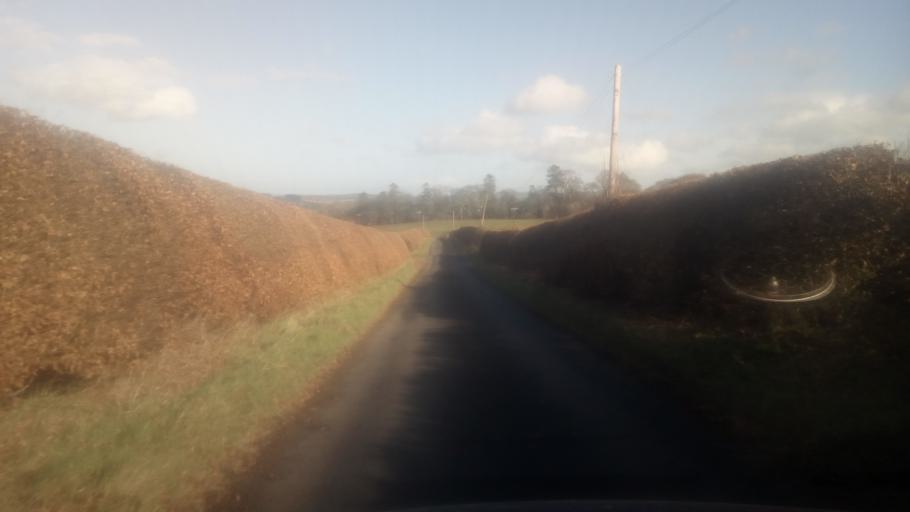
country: GB
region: Scotland
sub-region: The Scottish Borders
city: Jedburgh
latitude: 55.5047
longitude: -2.5030
